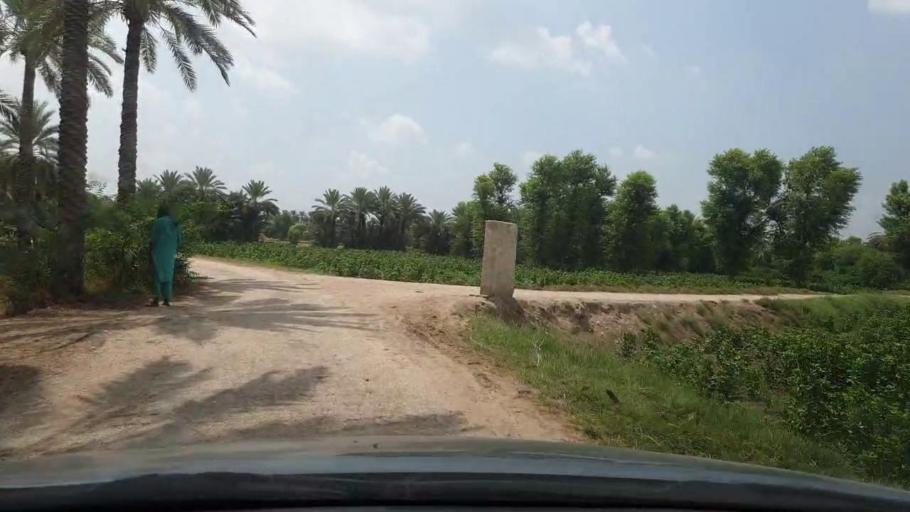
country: PK
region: Sindh
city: Kot Diji
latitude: 27.4061
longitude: 68.7495
